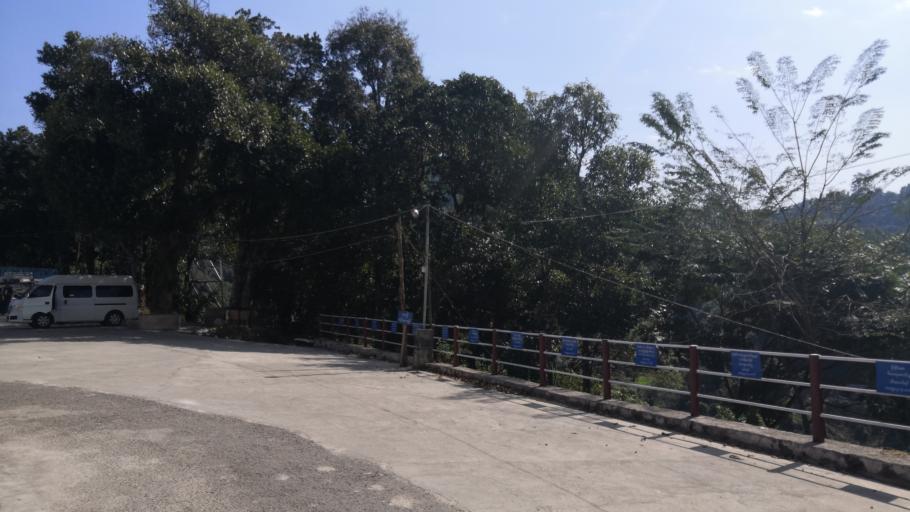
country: MM
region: Mandalay
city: Mogok
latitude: 22.9153
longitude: 96.5048
